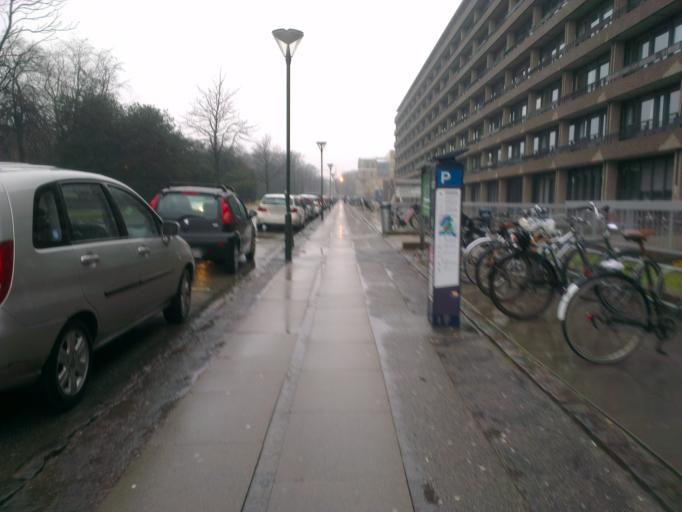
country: DK
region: Capital Region
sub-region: Kobenhavn
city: Copenhagen
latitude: 55.6948
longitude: 12.5667
